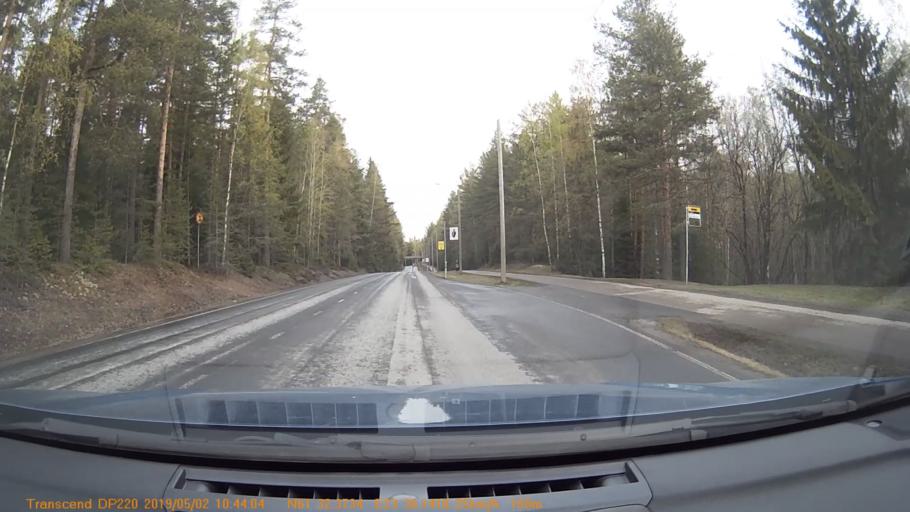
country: FI
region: Pirkanmaa
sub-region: Tampere
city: Yloejaervi
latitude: 61.5396
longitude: 23.6024
